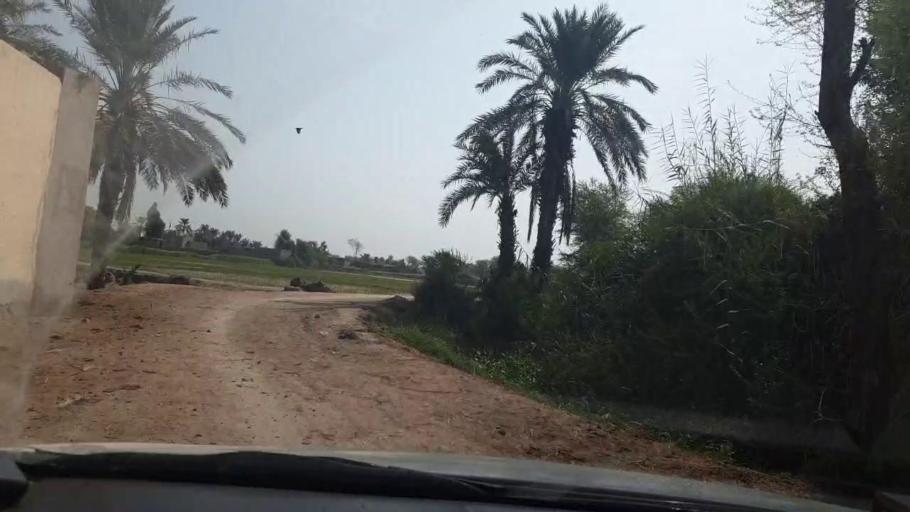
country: PK
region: Sindh
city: Chak
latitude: 27.8263
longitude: 68.7935
